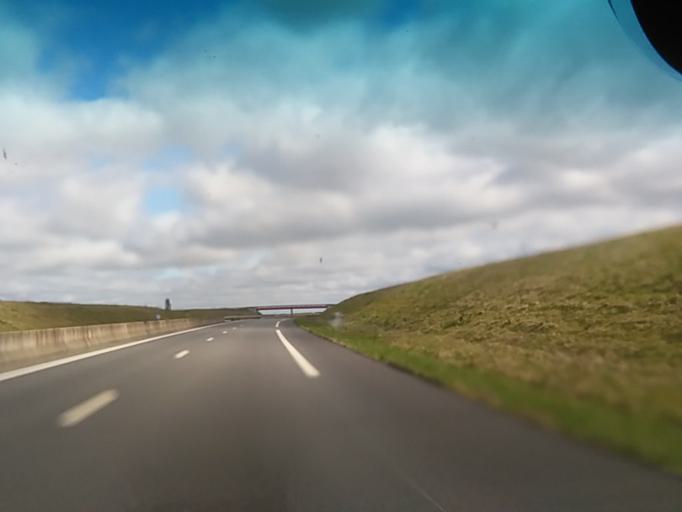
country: FR
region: Haute-Normandie
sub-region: Departement de l'Eure
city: Brionne
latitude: 49.1810
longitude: 0.7528
